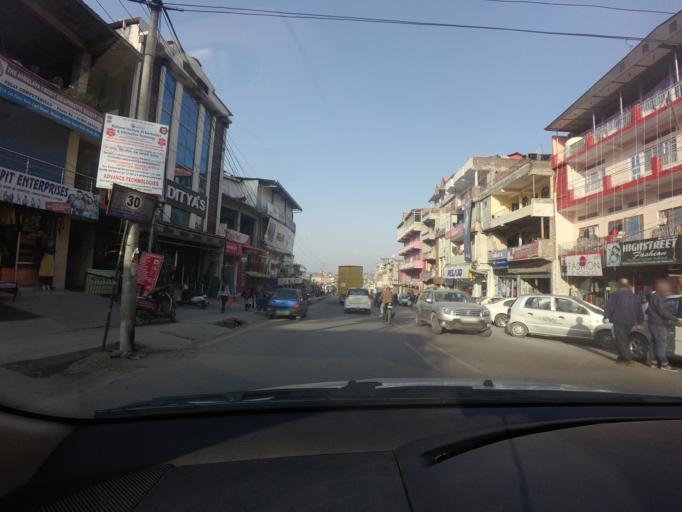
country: IN
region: Himachal Pradesh
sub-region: Mandi
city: Sundarnagar
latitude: 31.5332
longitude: 76.8890
